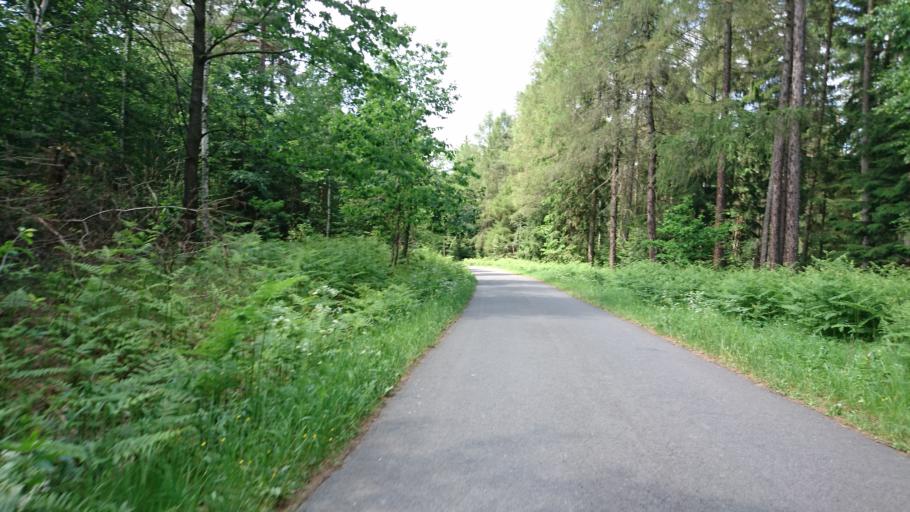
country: DE
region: Saxony
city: Bad Schandau
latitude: 50.8722
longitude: 14.1767
